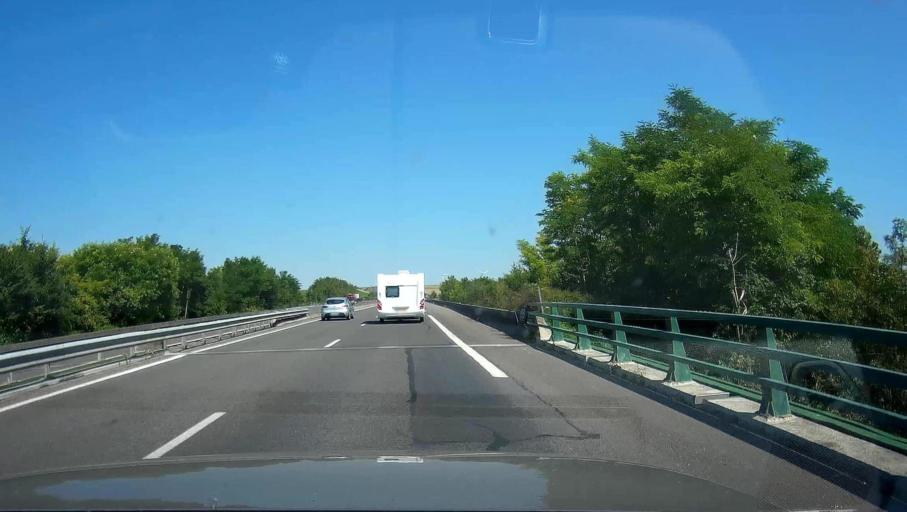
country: FR
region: Champagne-Ardenne
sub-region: Departement de l'Aube
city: Arcis-sur-Aube
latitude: 48.5441
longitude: 4.1888
